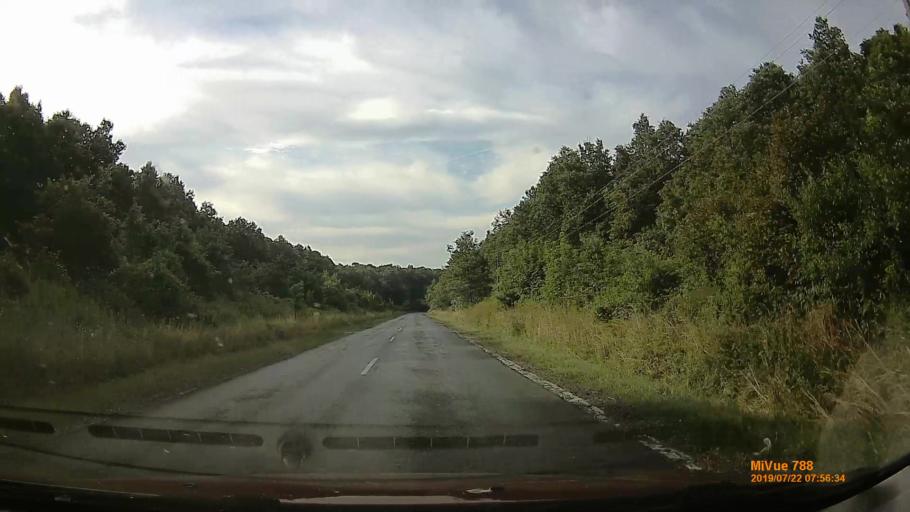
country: HU
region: Veszprem
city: Ajka
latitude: 47.0258
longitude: 17.5716
